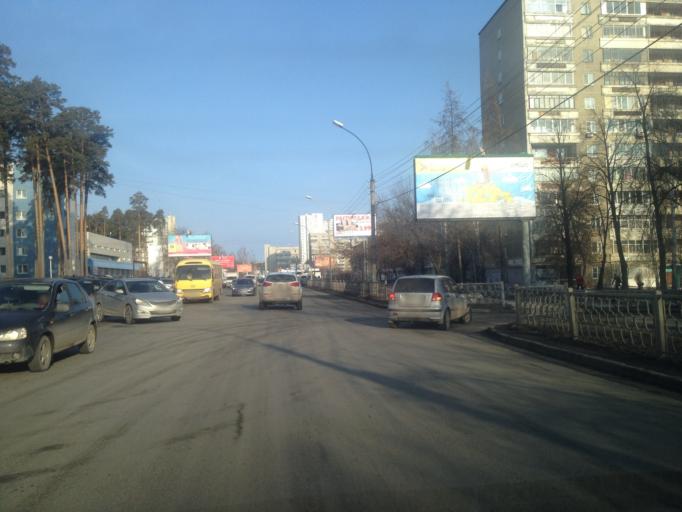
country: RU
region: Sverdlovsk
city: Sovkhoznyy
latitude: 56.8105
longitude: 60.5627
